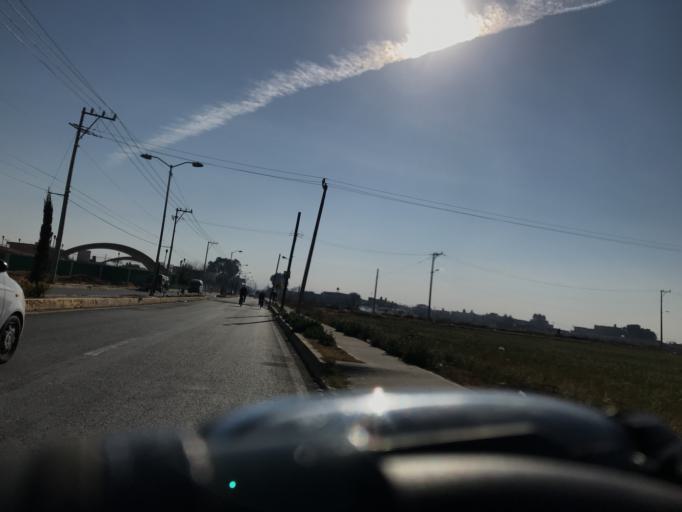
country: MX
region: Mexico
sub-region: Tonanitla
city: Colonia la Asuncion
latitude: 19.6938
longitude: -99.0666
